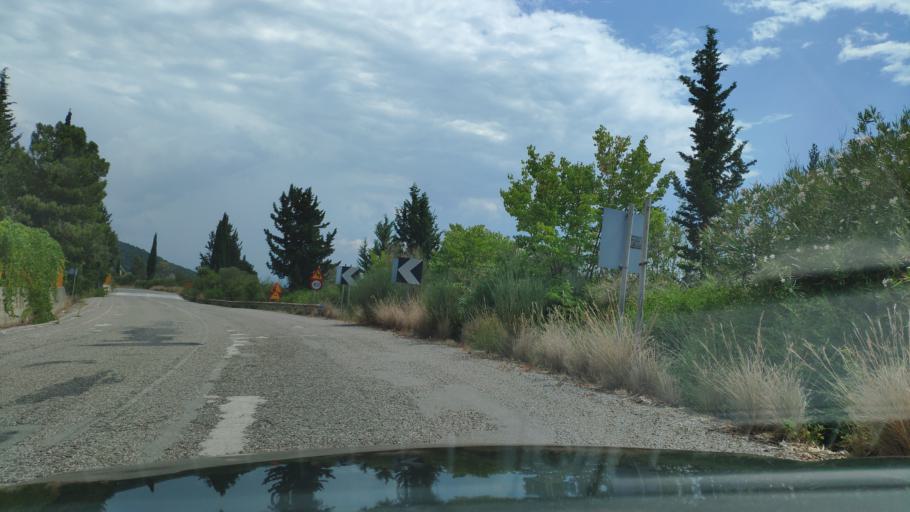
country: GR
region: West Greece
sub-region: Nomos Aitolias kai Akarnanias
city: Menidi
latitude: 39.0182
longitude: 21.1363
